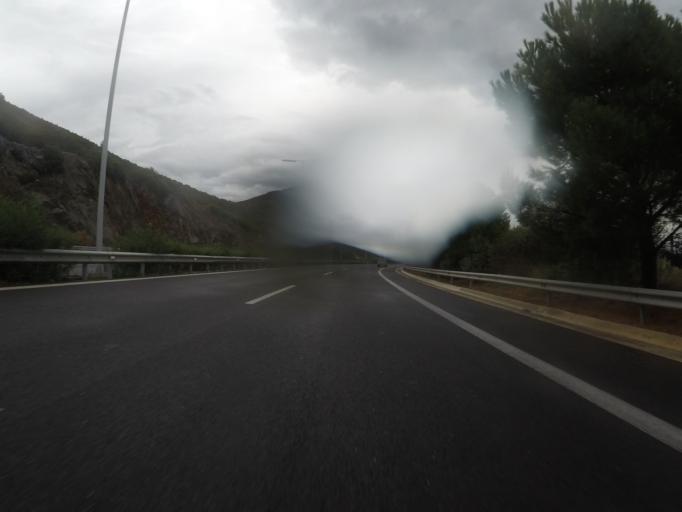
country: GR
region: Peloponnese
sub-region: Nomos Korinthias
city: Nemea
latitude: 37.7089
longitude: 22.5474
